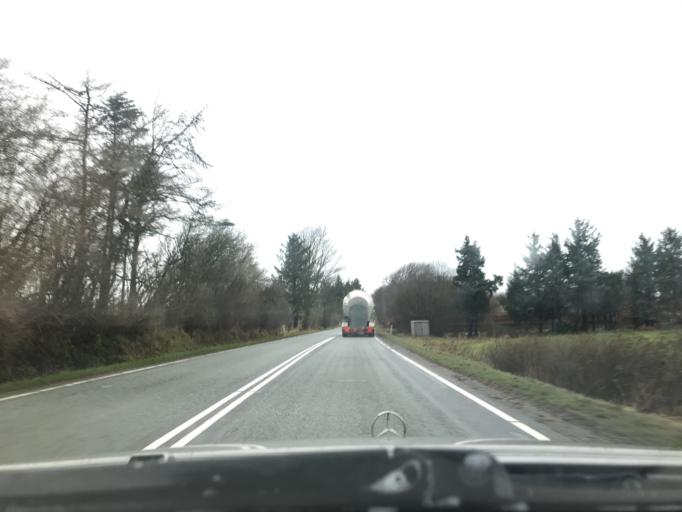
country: DK
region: South Denmark
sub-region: Esbjerg Kommune
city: Ribe
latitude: 55.2702
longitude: 8.8738
